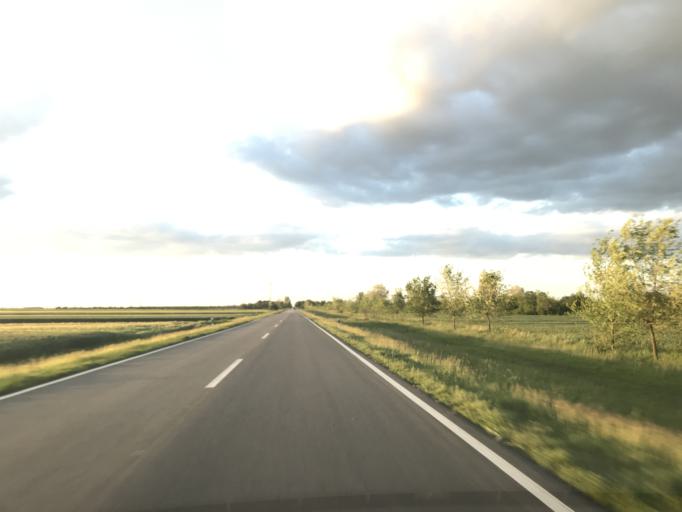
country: RS
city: Aleksandrovo
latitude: 45.6248
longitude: 20.5771
